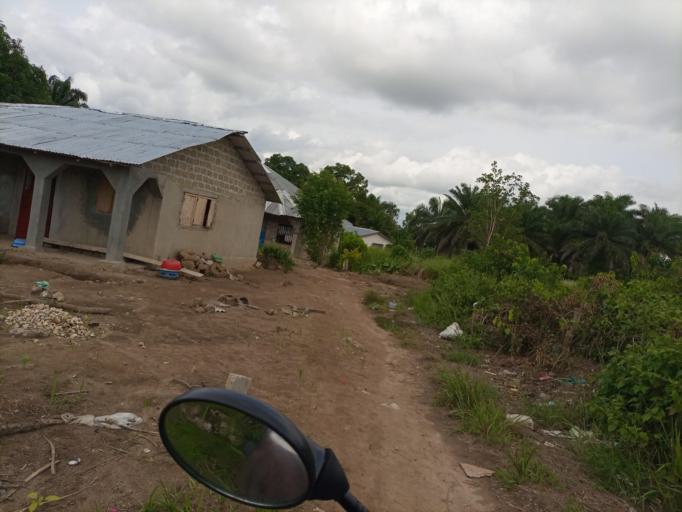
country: SL
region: Southern Province
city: Bo
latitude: 7.9694
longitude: -11.7683
